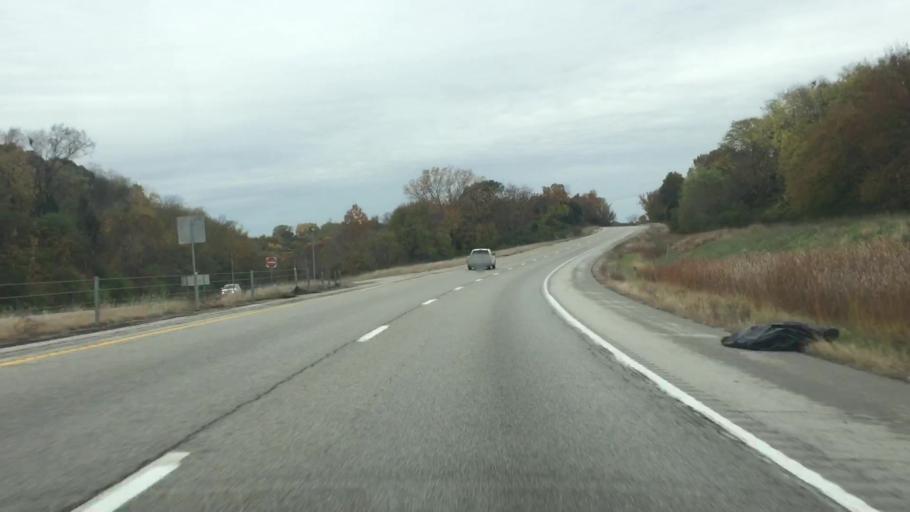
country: US
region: Missouri
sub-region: Jackson County
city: Lees Summit
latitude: 38.9518
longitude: -94.4153
